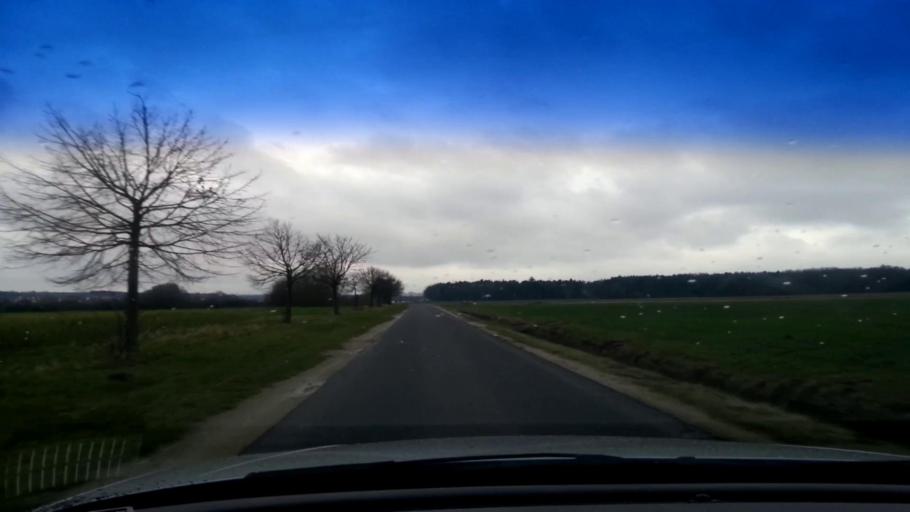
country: DE
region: Bavaria
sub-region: Upper Franconia
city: Frensdorf
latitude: 49.8236
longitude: 10.8257
